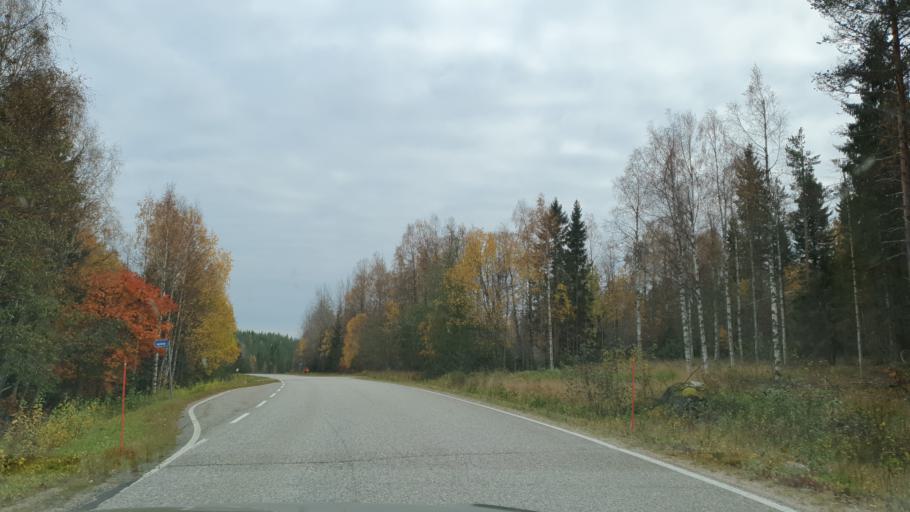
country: FI
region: Kainuu
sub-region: Kajaani
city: Ristijaervi
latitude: 64.4756
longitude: 28.2839
